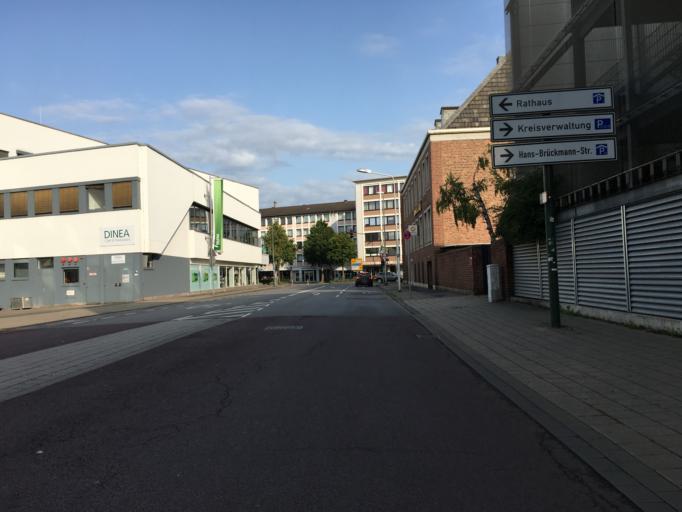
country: DE
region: North Rhine-Westphalia
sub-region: Regierungsbezirk Koln
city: Dueren
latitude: 50.8046
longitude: 6.4851
